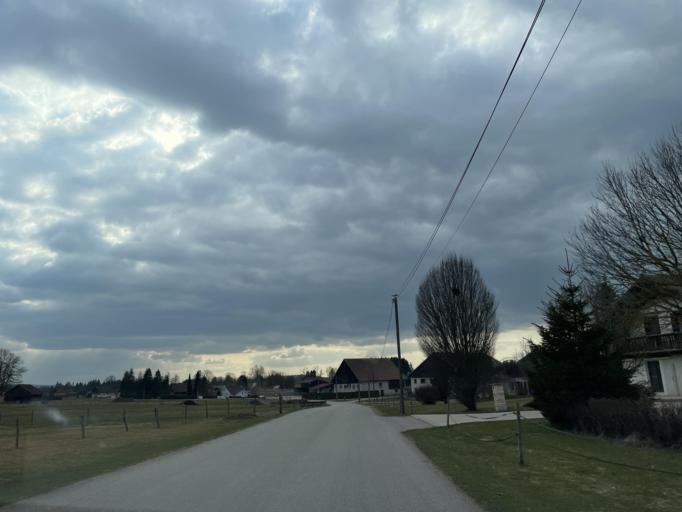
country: FR
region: Franche-Comte
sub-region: Departement du Doubs
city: Gilley
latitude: 47.0456
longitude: 6.5391
